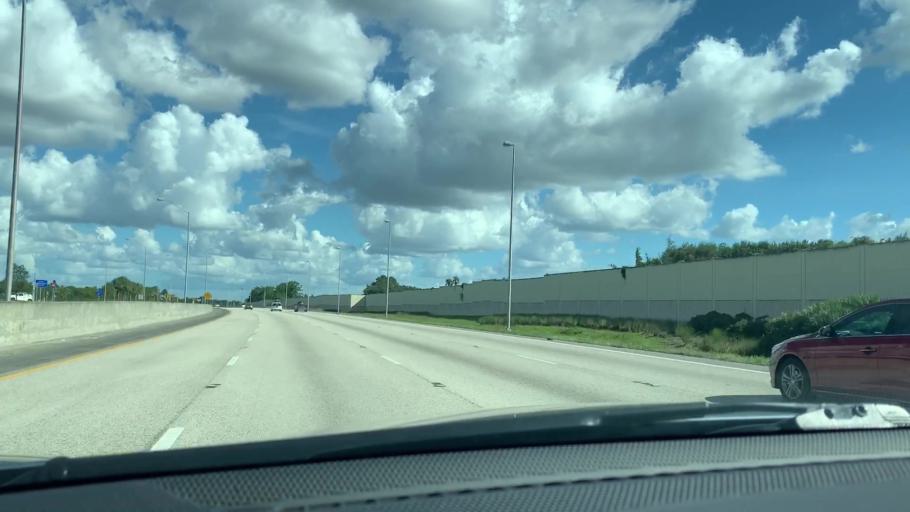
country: US
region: Florida
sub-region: Orange County
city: Gotha
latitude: 28.5129
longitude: -81.4990
